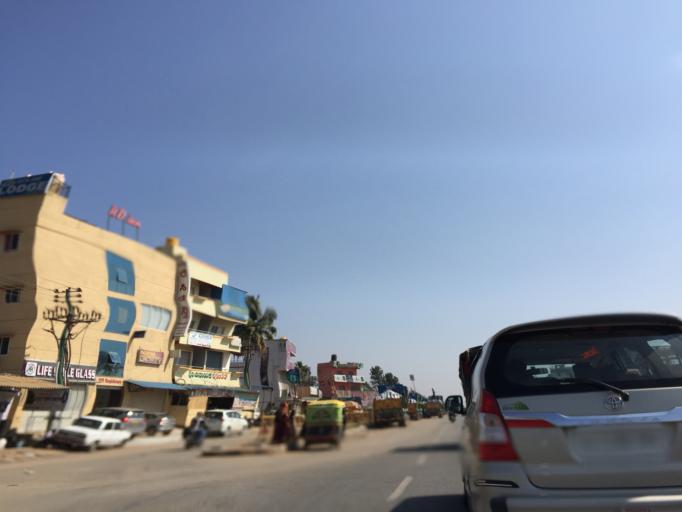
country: IN
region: Karnataka
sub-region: Bangalore Rural
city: Hoskote
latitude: 13.0743
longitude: 77.7908
